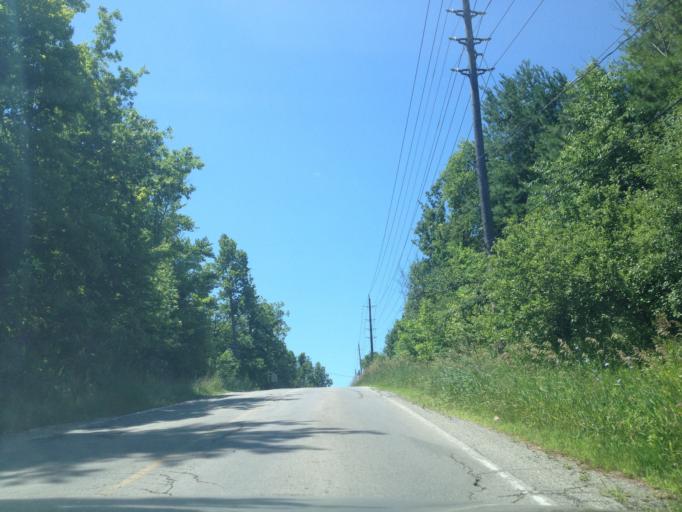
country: CA
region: Ontario
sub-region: Halton
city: Milton
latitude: 43.6595
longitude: -79.9552
